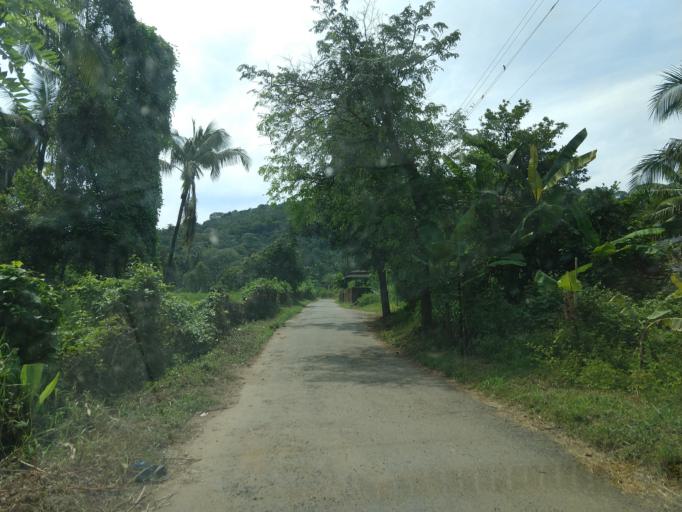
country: IN
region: Maharashtra
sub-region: Sindhudurg
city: Savantvadi
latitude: 15.9739
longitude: 73.7873
